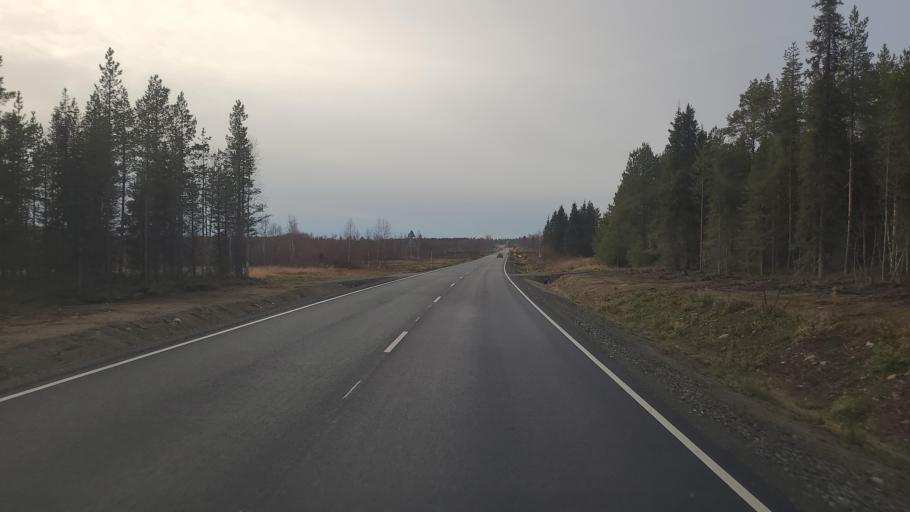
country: FI
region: Lapland
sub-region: Tunturi-Lappi
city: Kittilae
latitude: 67.8643
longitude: 24.9714
